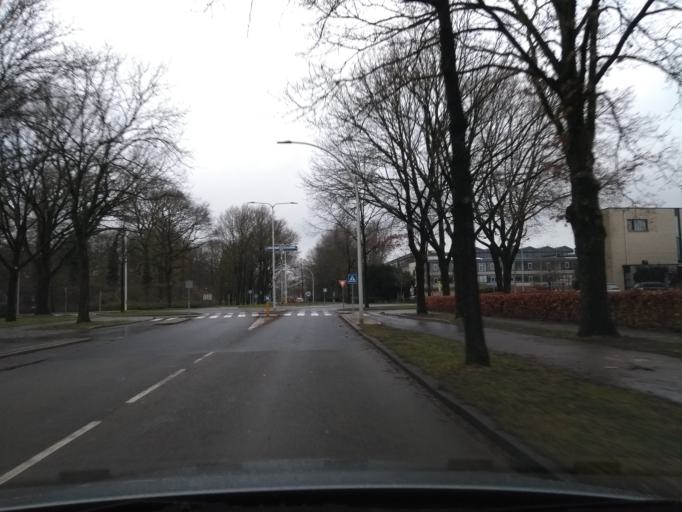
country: NL
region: Overijssel
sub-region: Gemeente Almelo
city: Almelo
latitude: 52.3682
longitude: 6.6620
